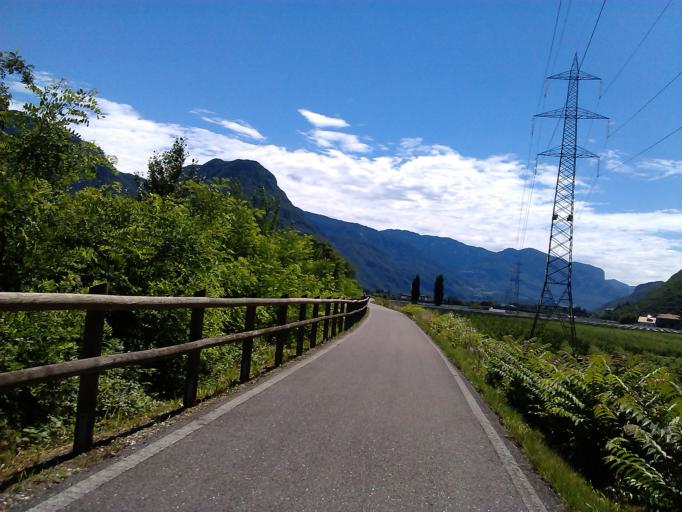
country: IT
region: Trentino-Alto Adige
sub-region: Bolzano
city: Vadena
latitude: 46.4271
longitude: 11.3100
